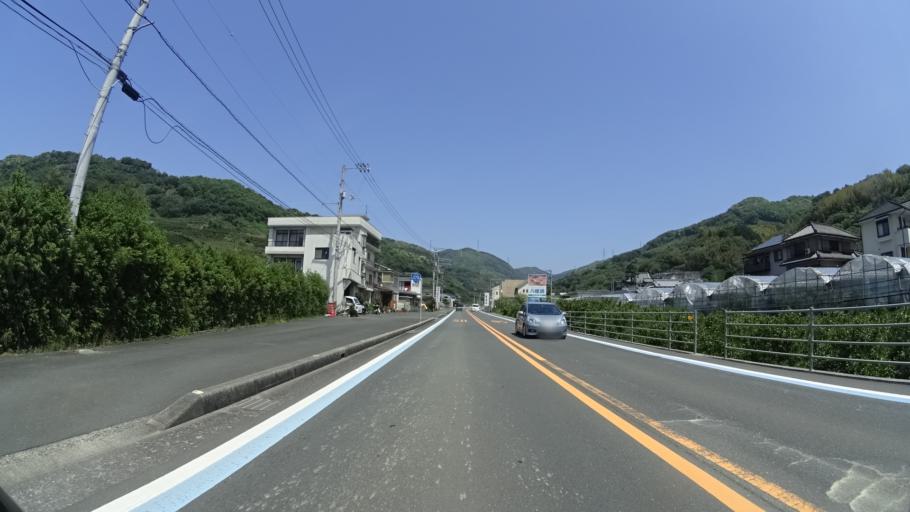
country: JP
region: Ehime
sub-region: Nishiuwa-gun
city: Ikata-cho
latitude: 33.4935
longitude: 132.3972
